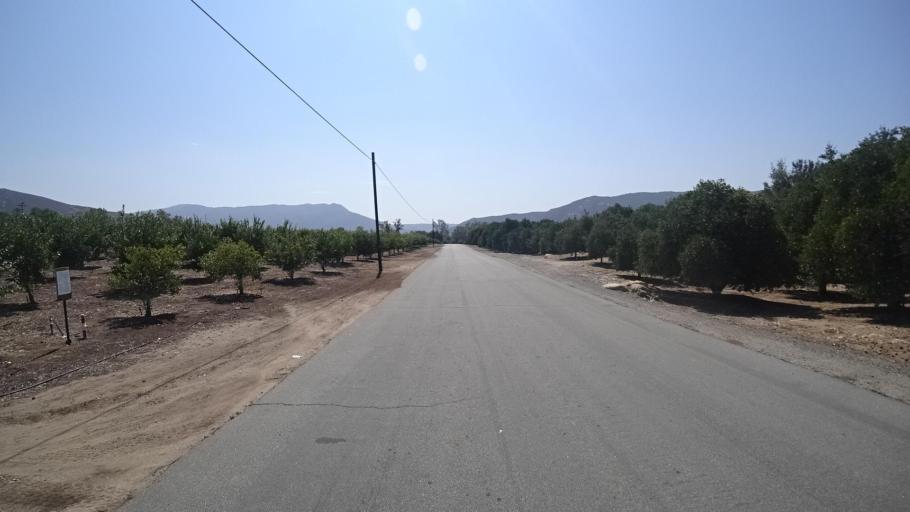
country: US
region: California
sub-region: San Diego County
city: Valley Center
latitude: 33.2915
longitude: -116.9593
